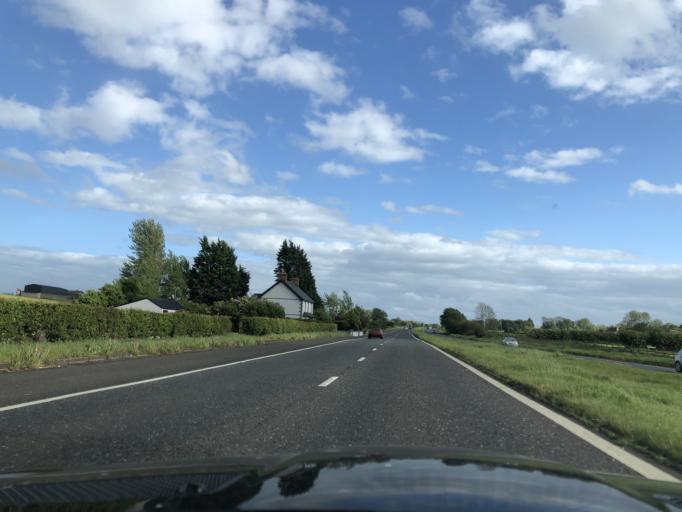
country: GB
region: Northern Ireland
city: Cullybackey
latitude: 54.9285
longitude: -6.3256
